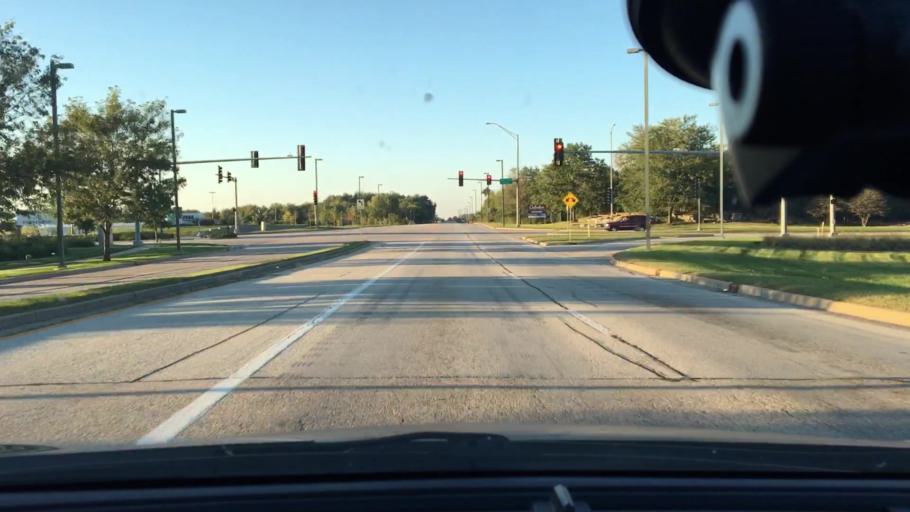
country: US
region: Illinois
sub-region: Kane County
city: East Dundee
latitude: 42.0697
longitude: -88.2236
